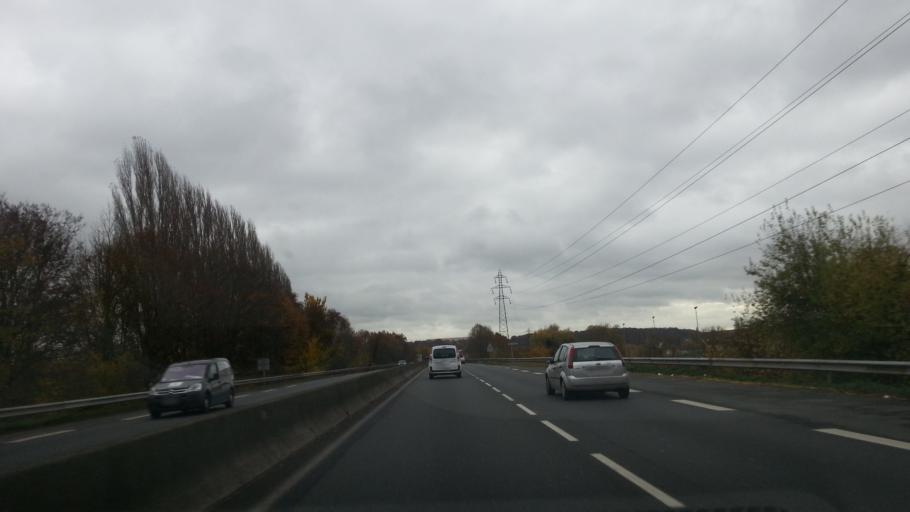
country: FR
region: Picardie
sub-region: Departement de l'Oise
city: Villers-Saint-Paul
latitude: 49.2800
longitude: 2.4811
